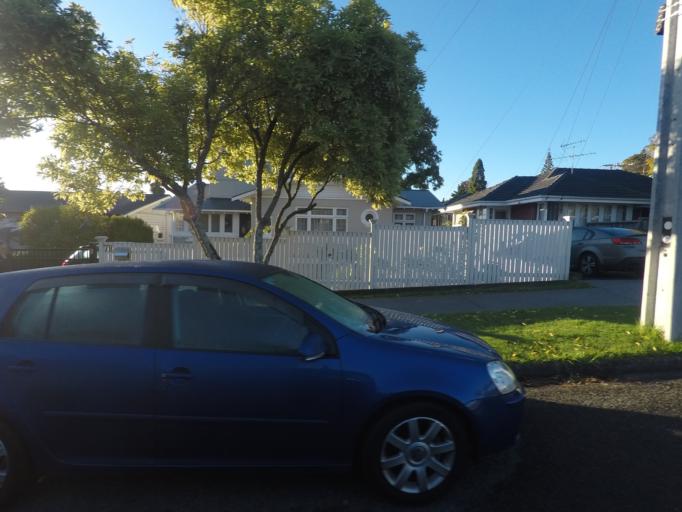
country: NZ
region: Auckland
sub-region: Auckland
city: Auckland
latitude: -36.8875
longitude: 174.7214
